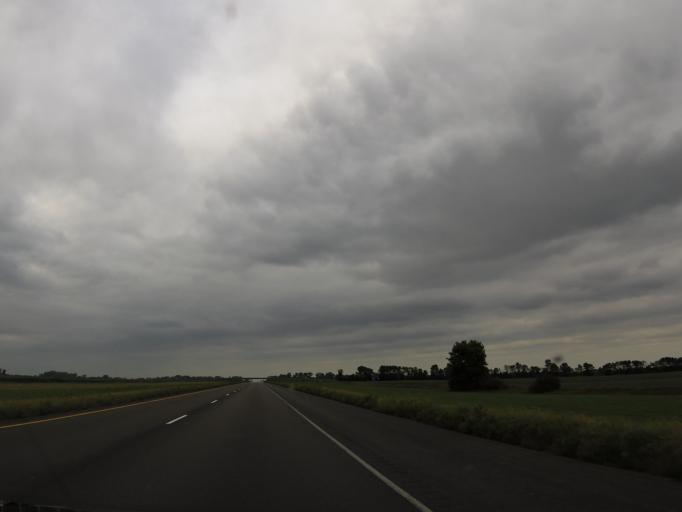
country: US
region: North Dakota
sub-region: Richland County
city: Wahpeton
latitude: 45.9861
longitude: -96.8359
